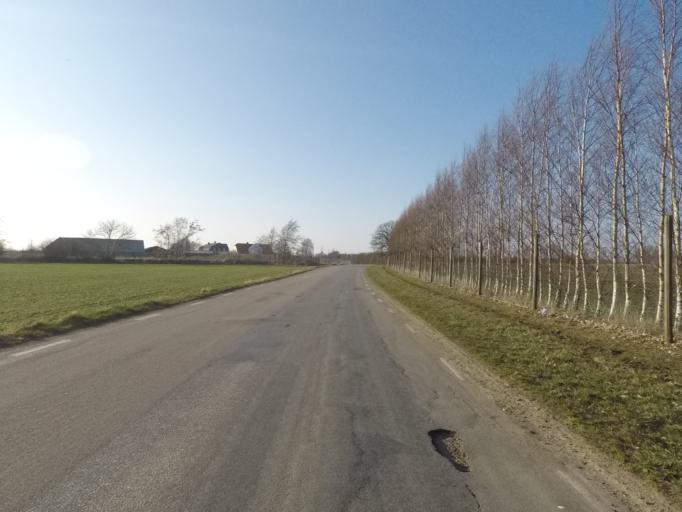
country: SE
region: Skane
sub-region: Hoganas Kommun
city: Hoganas
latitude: 56.2360
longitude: 12.6590
